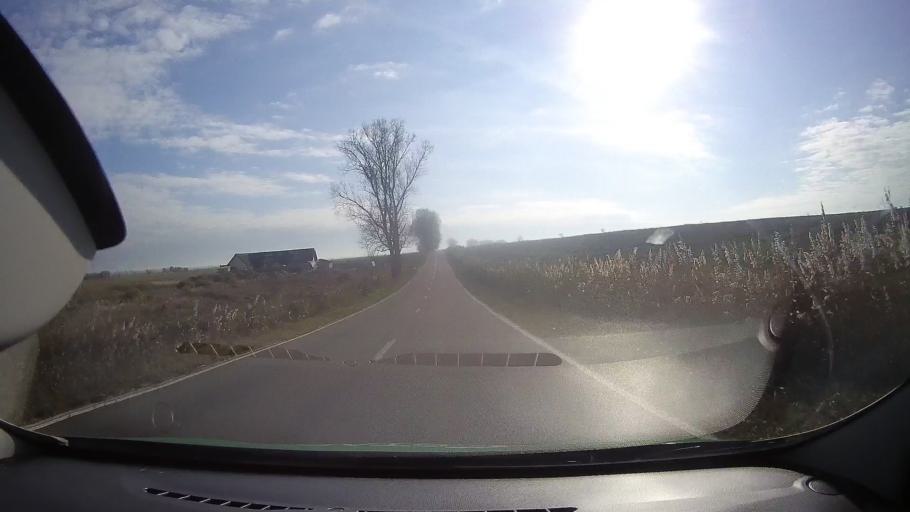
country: RO
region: Tulcea
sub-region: Comuna Mahmudia
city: Mahmudia
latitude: 45.0636
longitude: 29.1108
